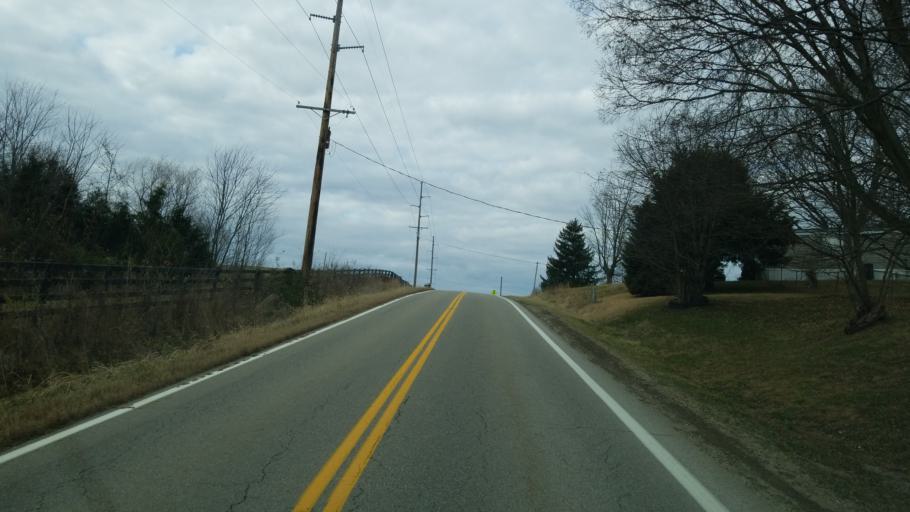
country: US
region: Ohio
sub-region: Ross County
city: Frankfort
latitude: 39.3529
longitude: -83.2372
